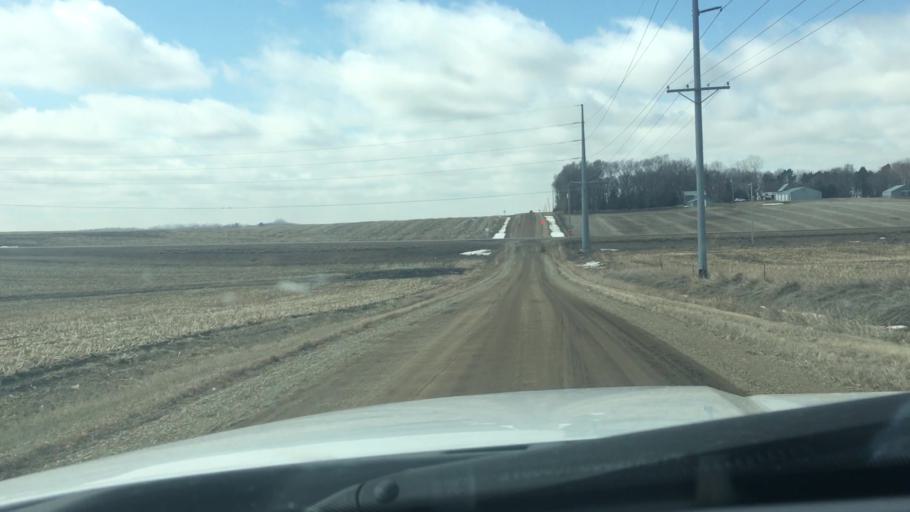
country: US
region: South Dakota
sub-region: Minnehaha County
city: Crooks
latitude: 43.6163
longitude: -96.8089
